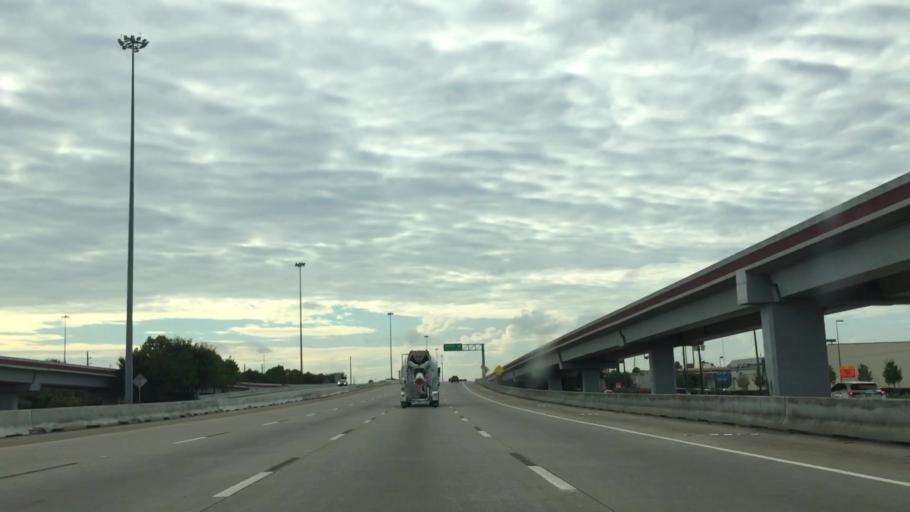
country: US
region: Texas
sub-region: Harris County
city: Jersey Village
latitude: 29.9632
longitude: -95.5506
